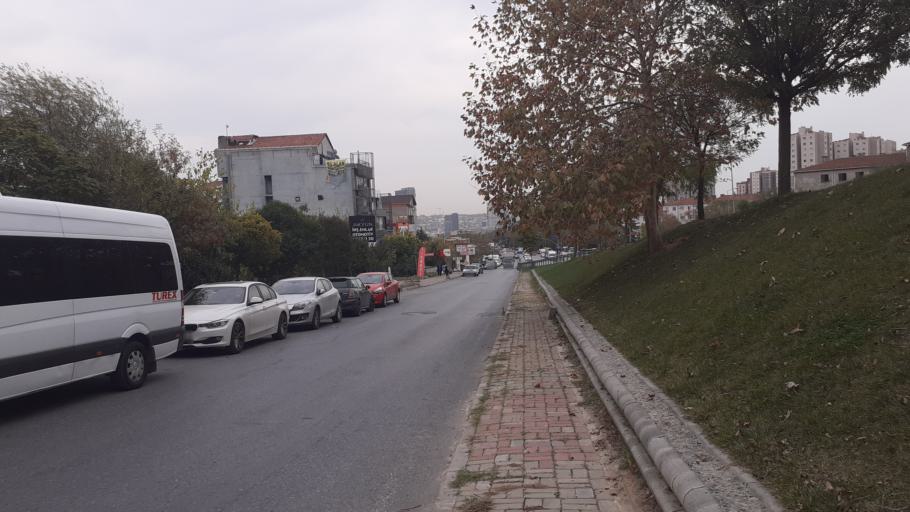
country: TR
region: Istanbul
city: Mahmutbey
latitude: 41.0501
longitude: 28.7960
